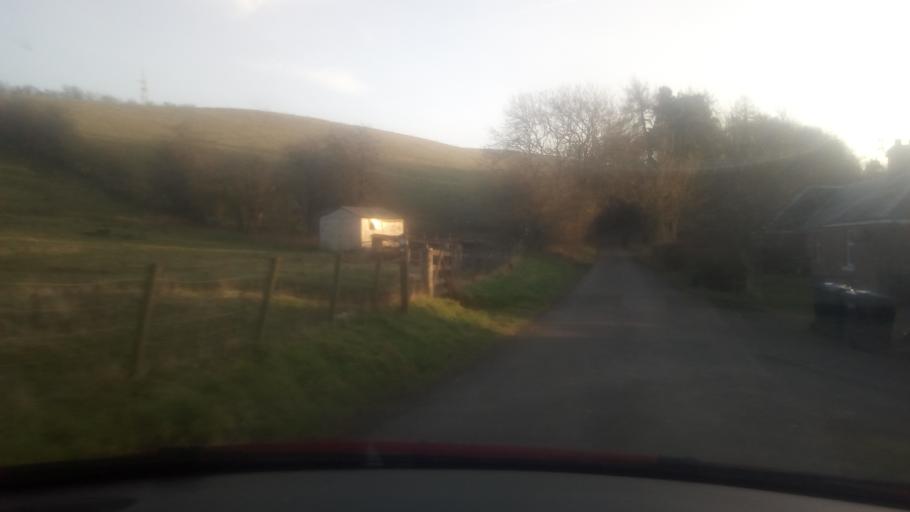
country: GB
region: Scotland
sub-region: The Scottish Borders
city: Jedburgh
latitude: 55.4974
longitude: -2.5412
